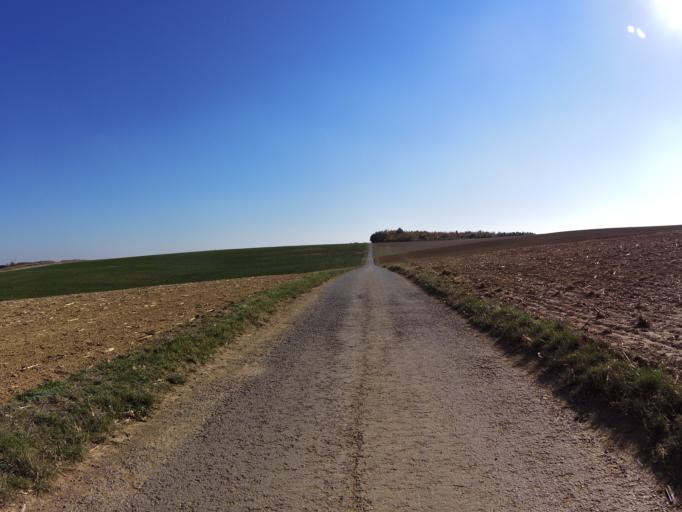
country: DE
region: Bavaria
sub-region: Regierungsbezirk Unterfranken
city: Eibelstadt
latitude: 49.7113
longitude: 9.9808
